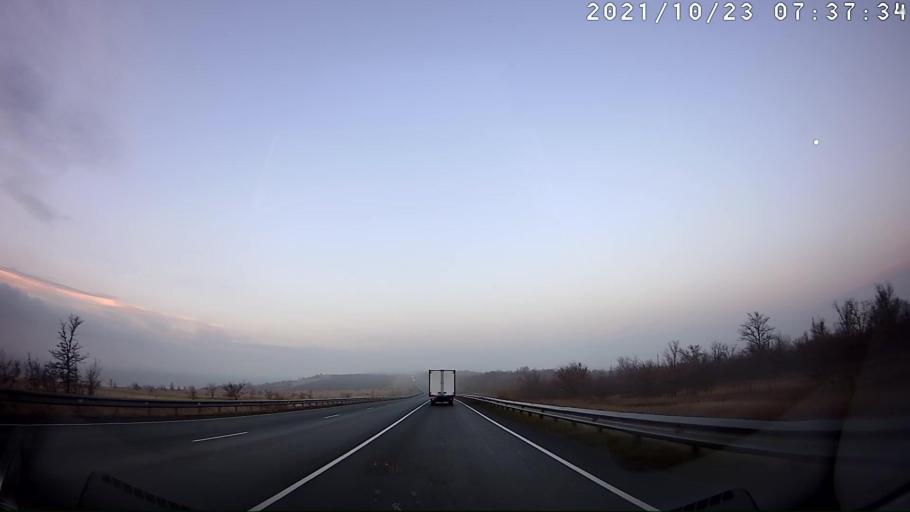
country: RU
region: Saratov
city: Alekseyevka
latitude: 52.2035
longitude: 47.8731
